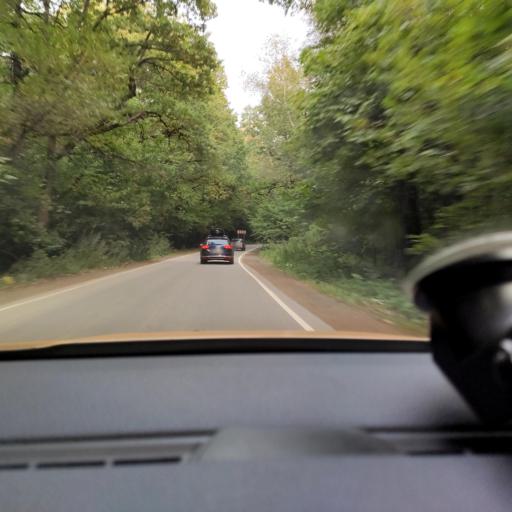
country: RU
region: Moscow
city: Vatutino
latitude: 55.9062
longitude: 37.6492
